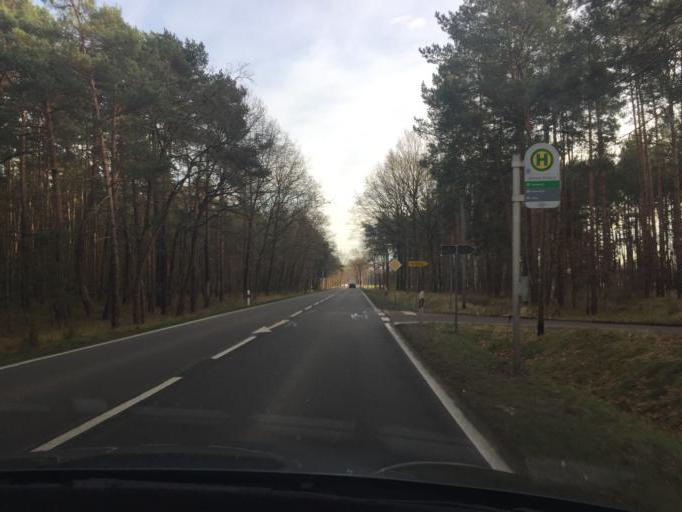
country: DE
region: Brandenburg
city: Cottbus
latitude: 51.7390
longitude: 14.4028
